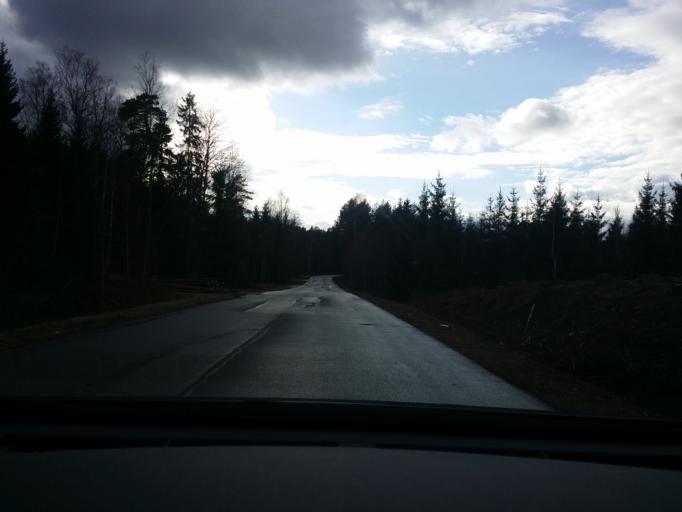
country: SE
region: Soedermanland
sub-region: Eskilstuna Kommun
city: Arla
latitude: 59.2947
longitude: 16.6974
